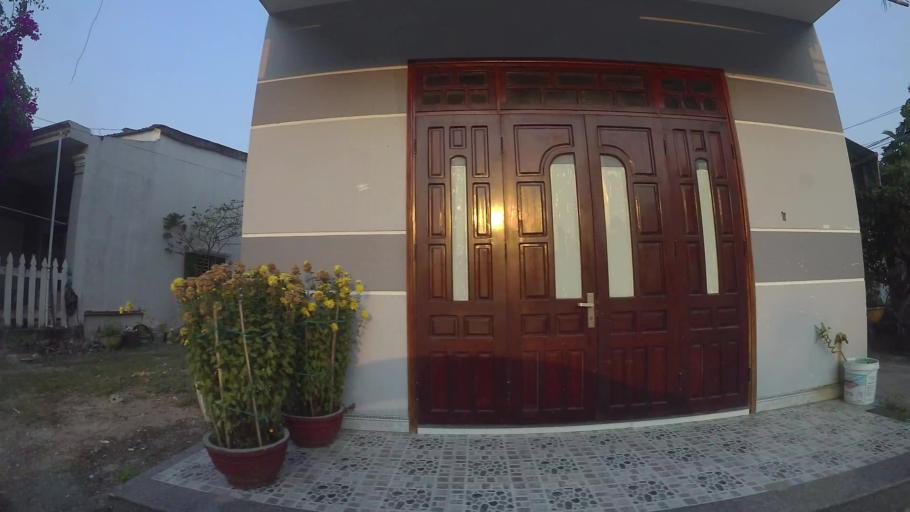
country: VN
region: Da Nang
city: Ngu Hanh Son
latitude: 15.9536
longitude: 108.2536
